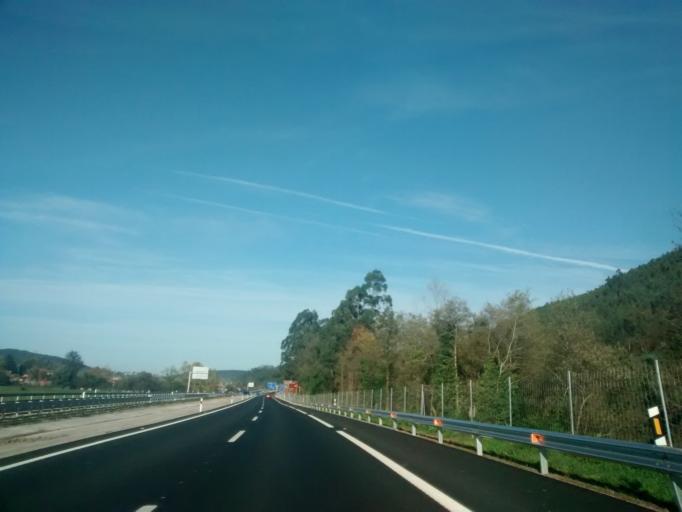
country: ES
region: Cantabria
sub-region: Provincia de Cantabria
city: Puente Viesgo
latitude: 43.3211
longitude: -3.9529
